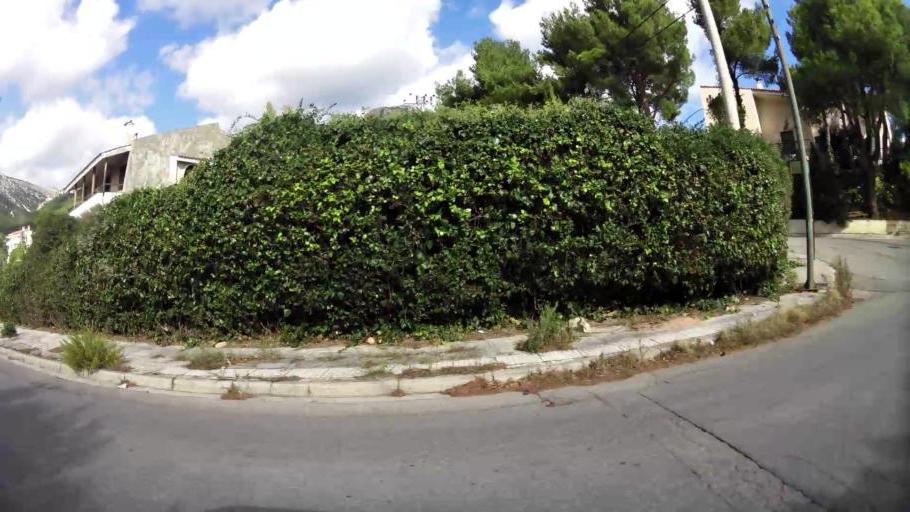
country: GR
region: Attica
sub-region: Nomarchia Anatolikis Attikis
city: Thrakomakedones
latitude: 38.1396
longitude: 23.7545
